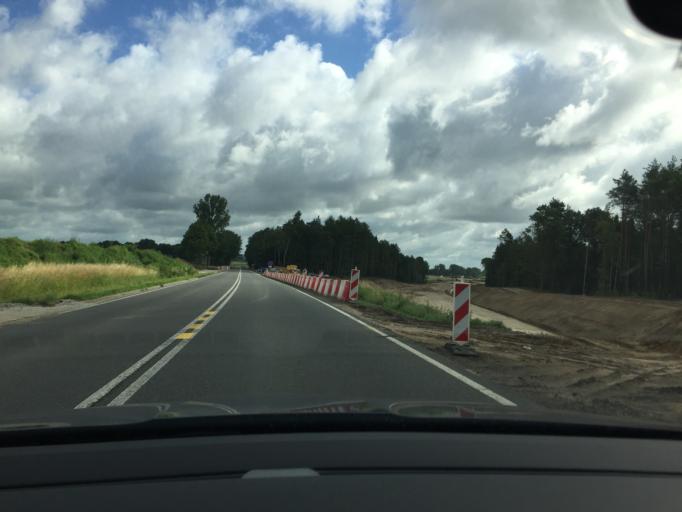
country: PL
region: West Pomeranian Voivodeship
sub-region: Powiat gryficki
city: Ploty
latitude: 53.8432
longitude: 15.3116
